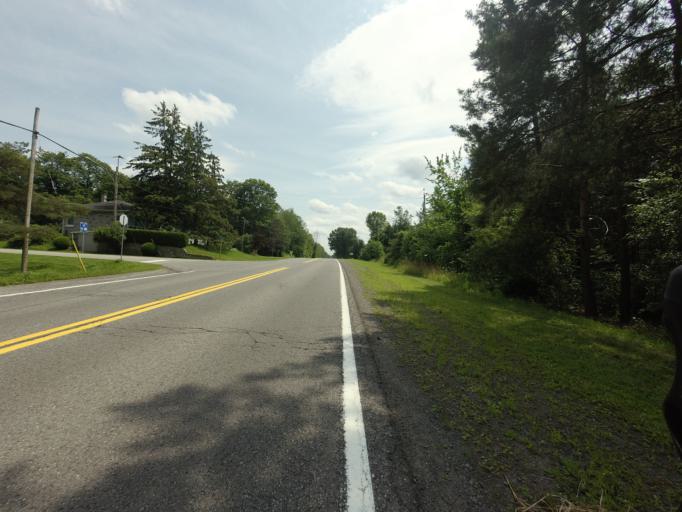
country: CA
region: Ontario
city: Ottawa
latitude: 45.2808
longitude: -75.6287
